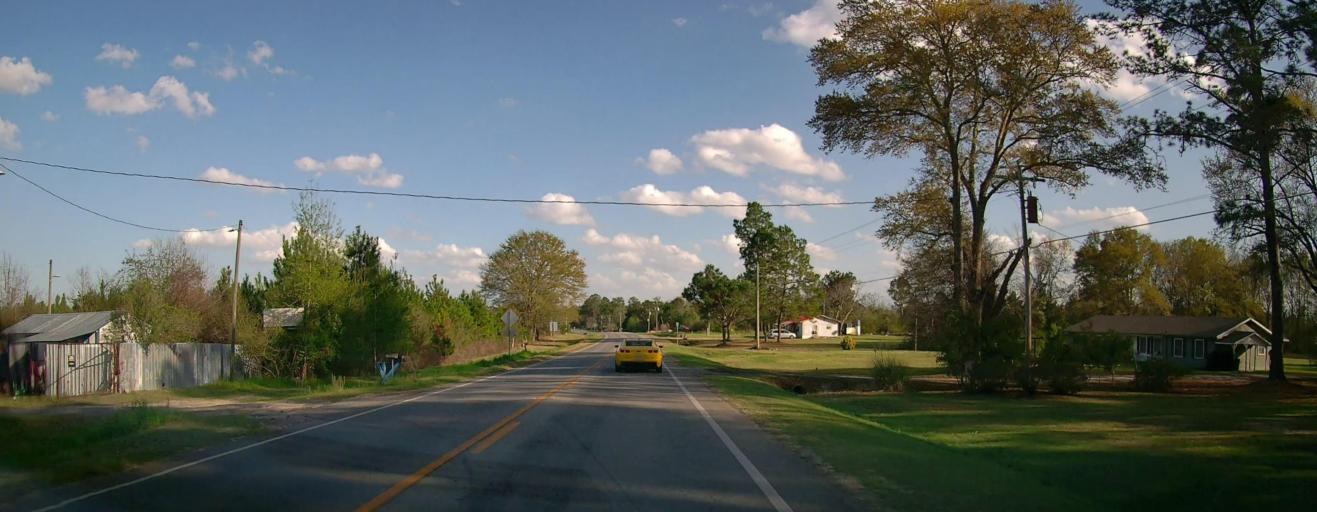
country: US
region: Georgia
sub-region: Toombs County
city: Lyons
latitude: 32.1875
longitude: -82.3017
